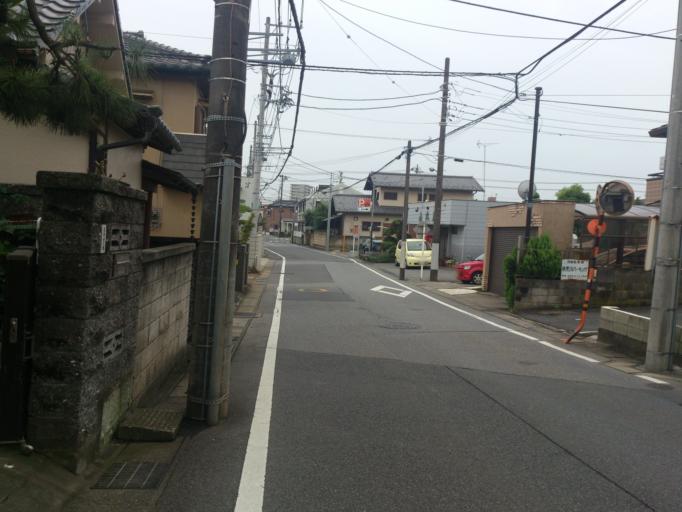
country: JP
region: Chiba
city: Chiba
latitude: 35.6529
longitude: 140.0655
